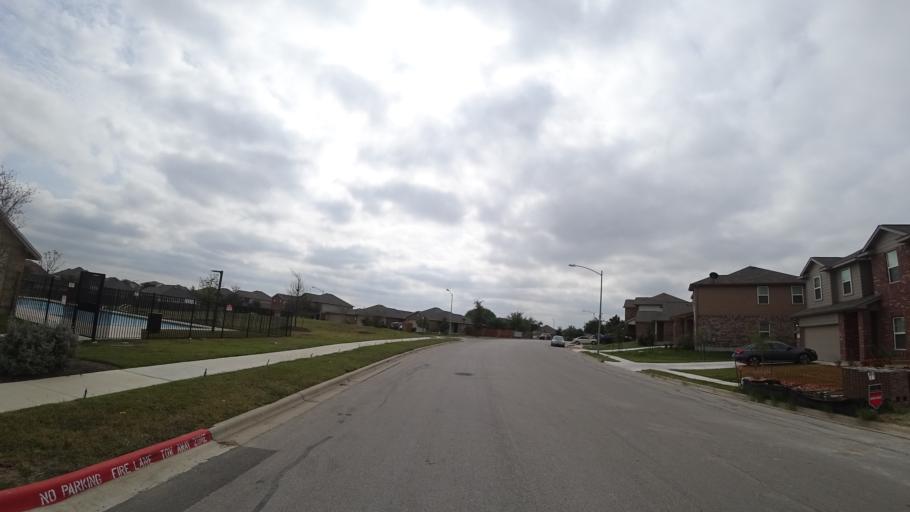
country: US
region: Texas
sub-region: Travis County
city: Pflugerville
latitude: 30.3912
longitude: -97.6188
